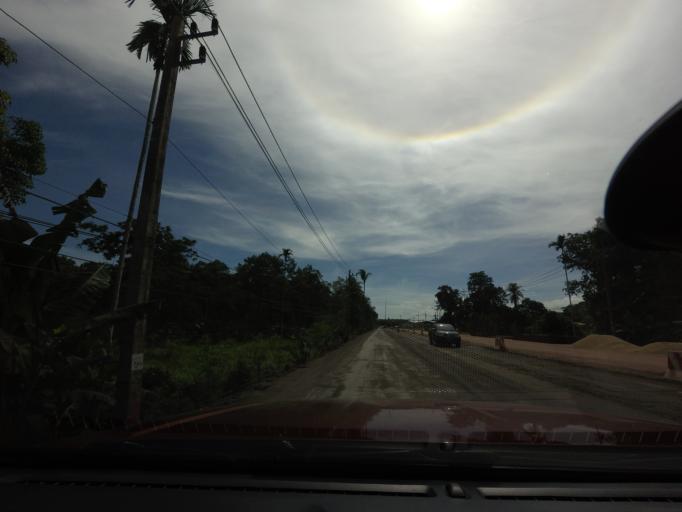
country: TH
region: Yala
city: Raman
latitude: 6.4766
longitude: 101.4395
